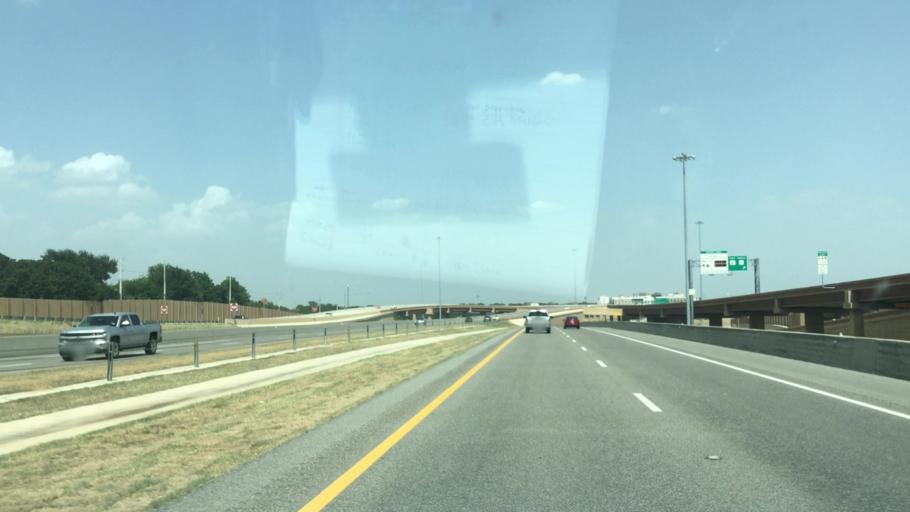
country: US
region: Texas
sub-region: Tarrant County
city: Bedford
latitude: 32.8400
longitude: -97.1579
